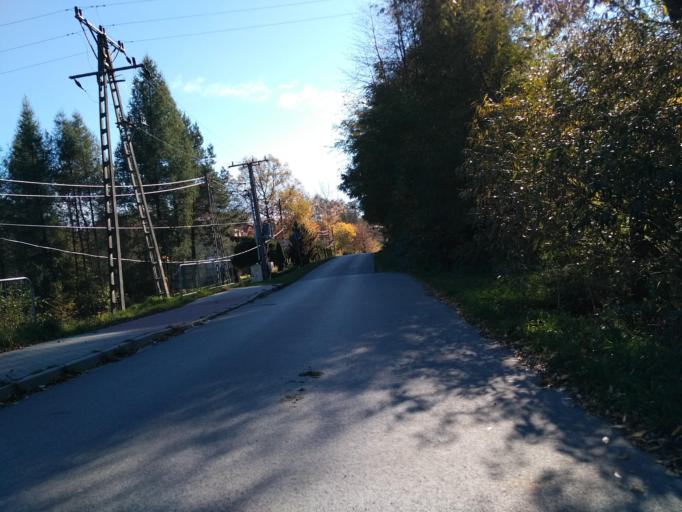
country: PL
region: Subcarpathian Voivodeship
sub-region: Powiat ropczycko-sedziszowski
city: Iwierzyce
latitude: 49.9830
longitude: 21.7261
